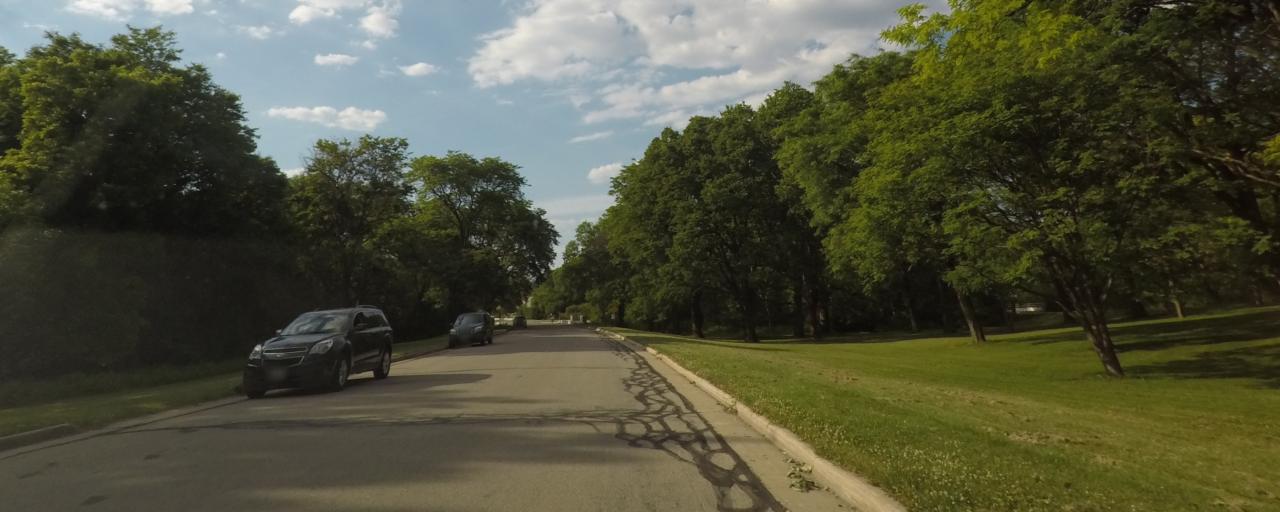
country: US
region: Wisconsin
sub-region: Milwaukee County
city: Hales Corners
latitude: 42.9287
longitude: -88.0292
